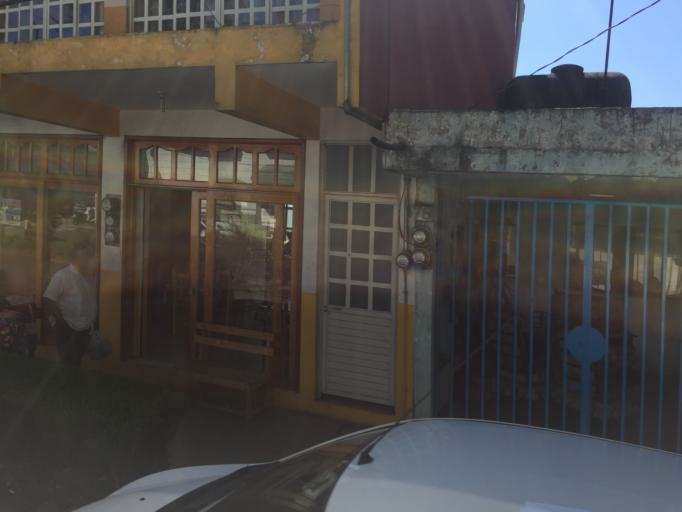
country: MX
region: Veracruz
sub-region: Xalapa
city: Xalapa de Enriquez
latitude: 19.5418
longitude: -96.9236
